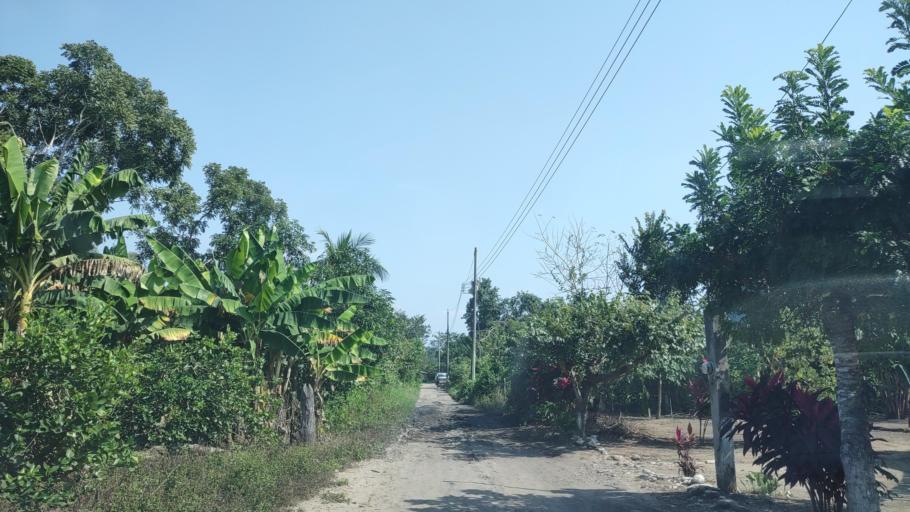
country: MX
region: Puebla
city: Espinal
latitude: 20.2612
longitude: -97.3090
